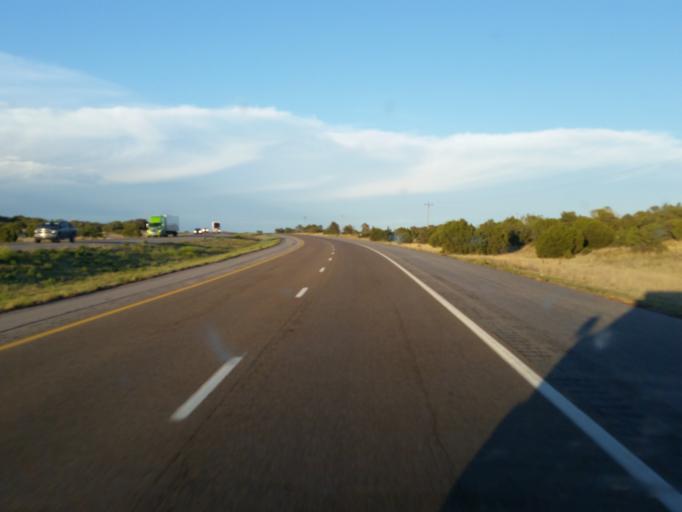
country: US
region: New Mexico
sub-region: Torrance County
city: Moriarty
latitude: 35.0019
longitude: -105.5551
